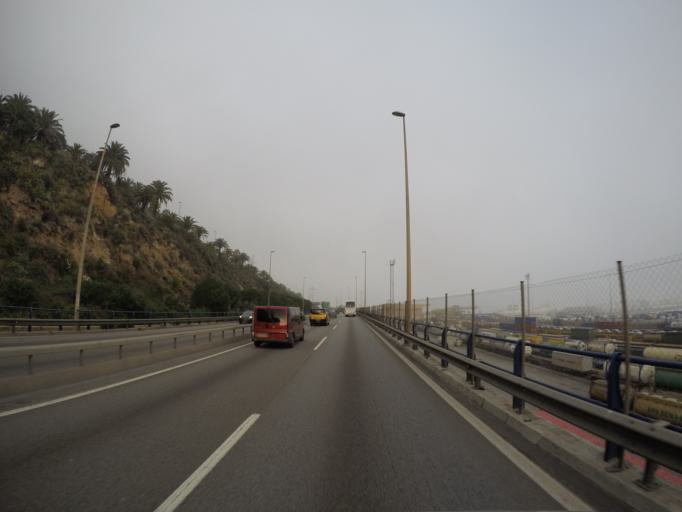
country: ES
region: Catalonia
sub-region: Provincia de Barcelona
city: Ciutat Vella
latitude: 41.3644
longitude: 2.1708
